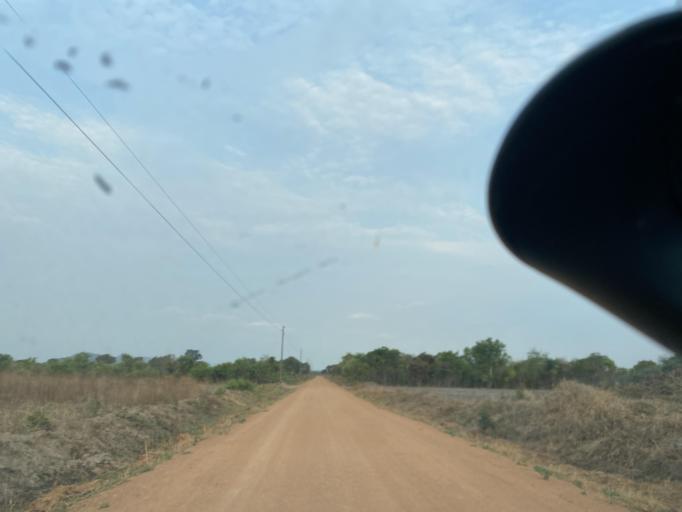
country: ZM
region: Lusaka
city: Chongwe
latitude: -15.1940
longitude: 28.5772
